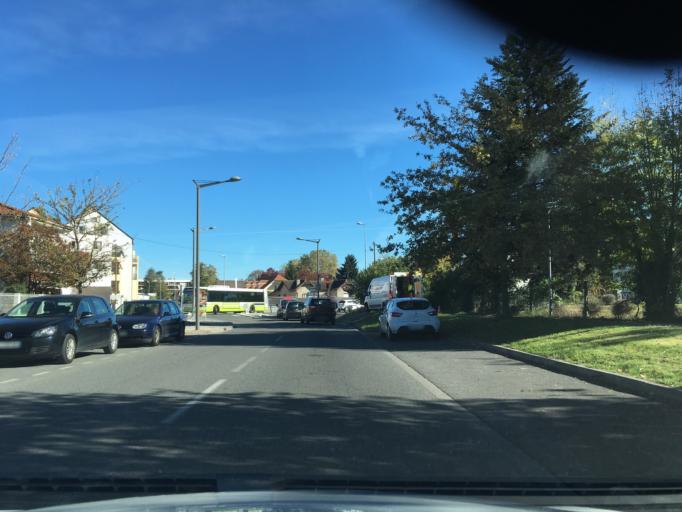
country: FR
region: Aquitaine
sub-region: Departement des Pyrenees-Atlantiques
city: Pau
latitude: 43.3191
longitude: -0.3493
